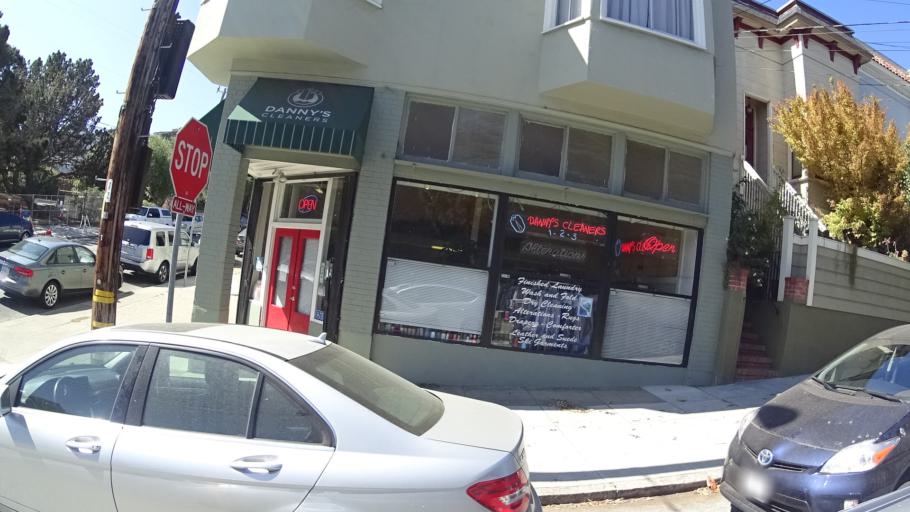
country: US
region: California
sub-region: San Francisco County
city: San Francisco
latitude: 37.7520
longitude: -122.4386
